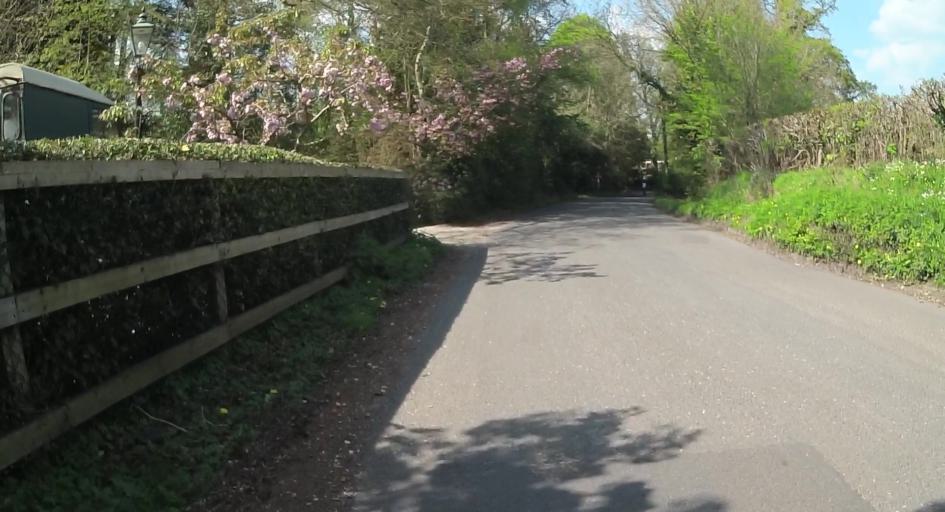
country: GB
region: England
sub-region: Hampshire
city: Tadley
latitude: 51.3522
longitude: -1.0972
